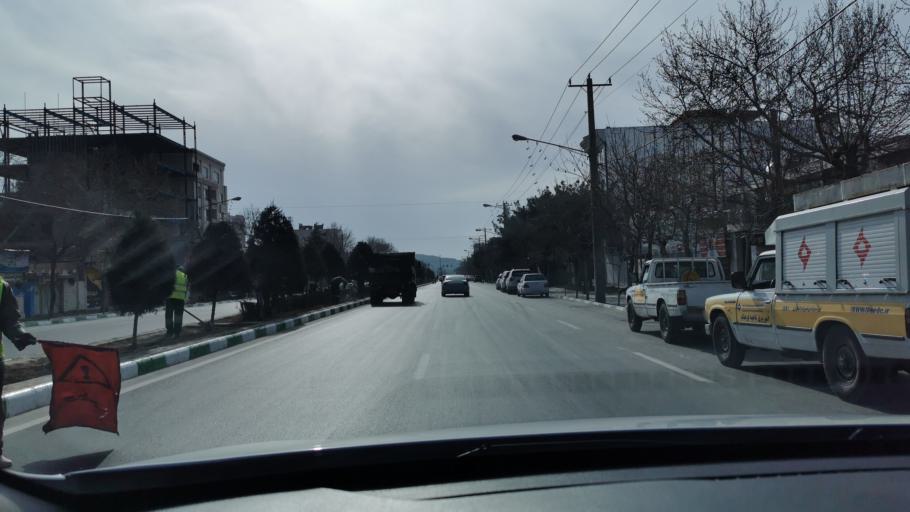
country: IR
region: Razavi Khorasan
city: Mashhad
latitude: 36.2890
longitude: 59.5411
